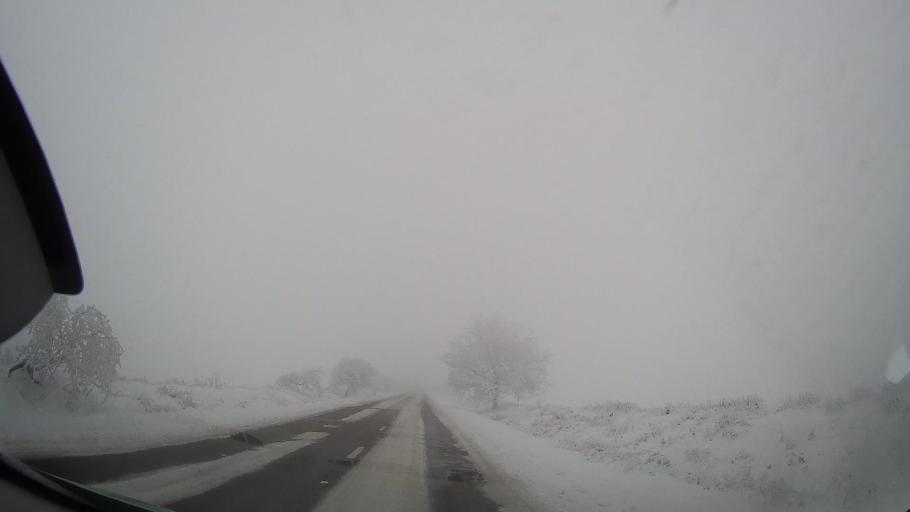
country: RO
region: Neamt
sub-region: Comuna Valea Ursului
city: Valea Ursului
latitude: 46.8196
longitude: 27.0644
